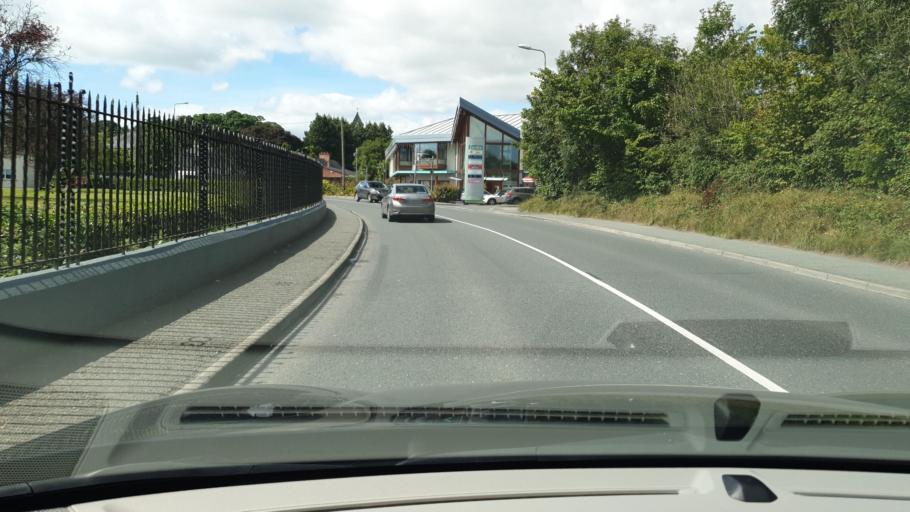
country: IE
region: Leinster
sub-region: An Mhi
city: Ratoath
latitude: 53.5065
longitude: -6.4575
